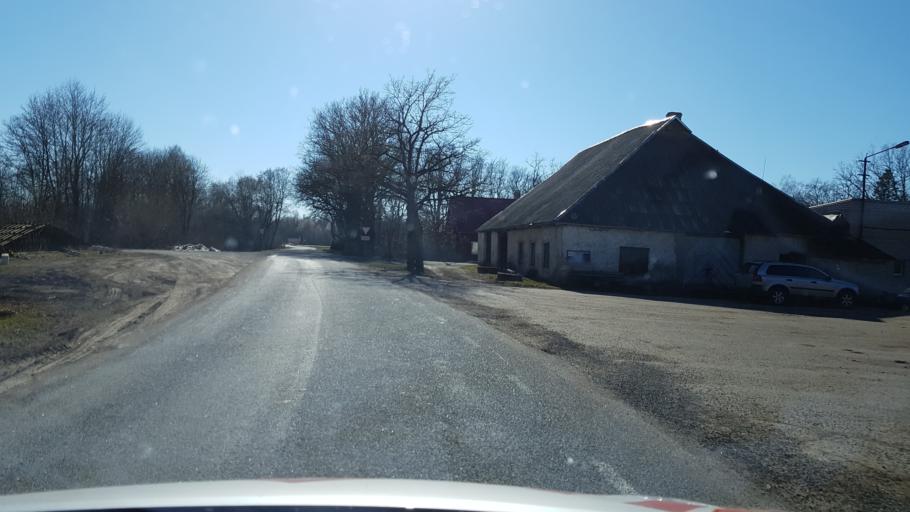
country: EE
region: Laeaene-Virumaa
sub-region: Someru vald
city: Someru
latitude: 59.3666
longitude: 26.4452
